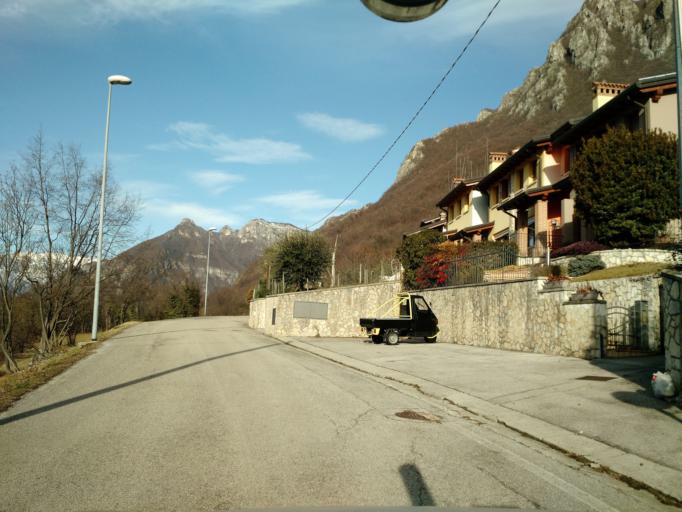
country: IT
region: Veneto
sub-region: Provincia di Vicenza
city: Cogollo del Cengio
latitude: 45.7956
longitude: 11.3981
